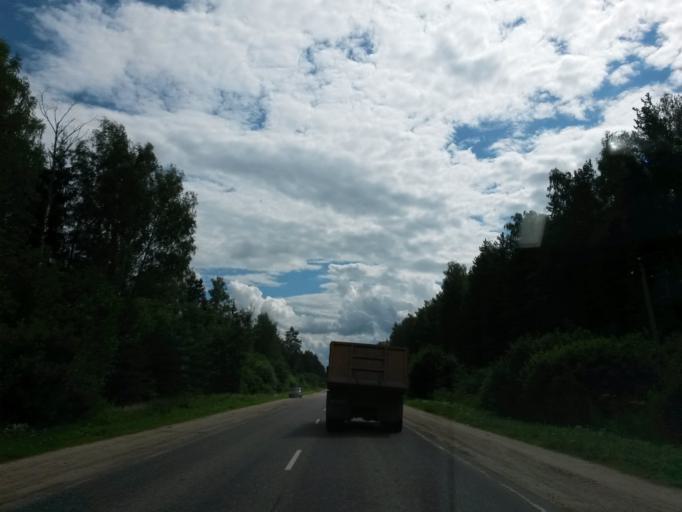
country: RU
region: Ivanovo
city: Novo-Talitsy
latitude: 57.0515
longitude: 40.7353
